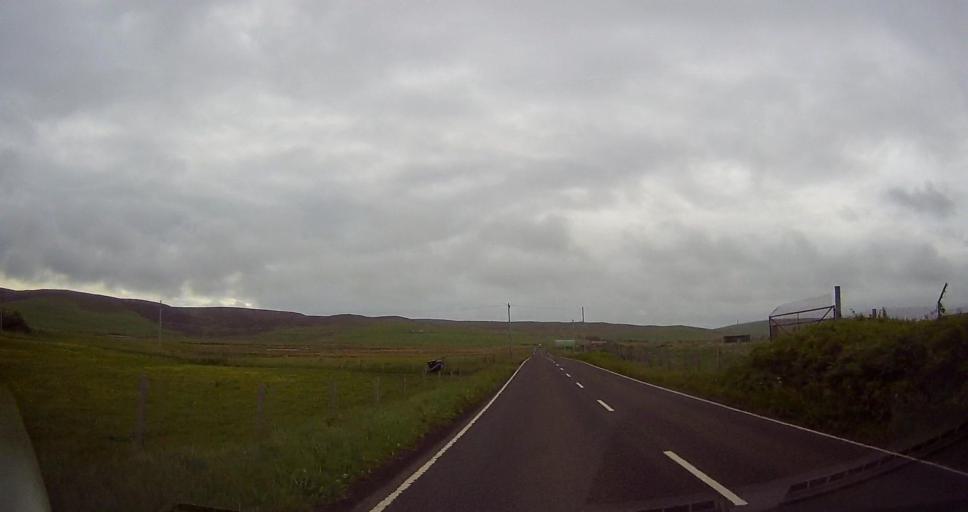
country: GB
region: Scotland
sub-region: Orkney Islands
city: Stromness
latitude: 59.0246
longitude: -3.1671
